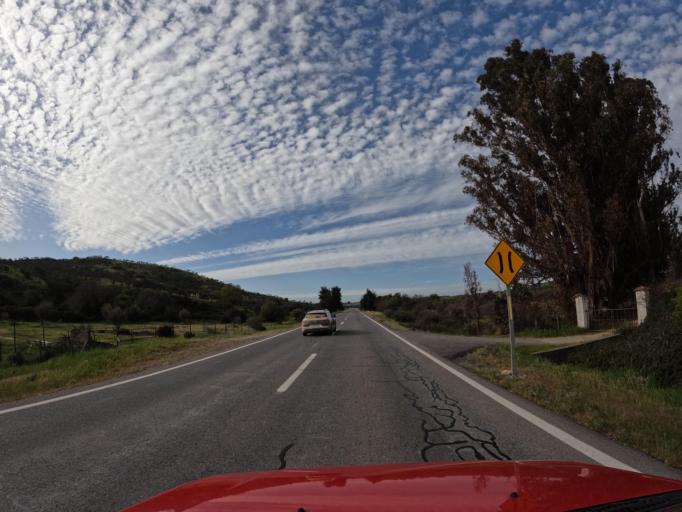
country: CL
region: O'Higgins
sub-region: Provincia de Colchagua
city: Santa Cruz
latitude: -34.2922
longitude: -71.7305
